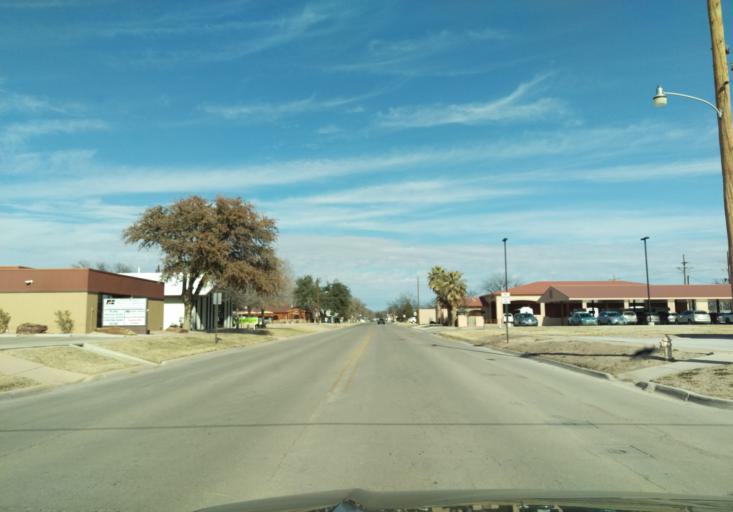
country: US
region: New Mexico
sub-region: Eddy County
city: Carlsbad
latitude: 32.4250
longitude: -104.2264
